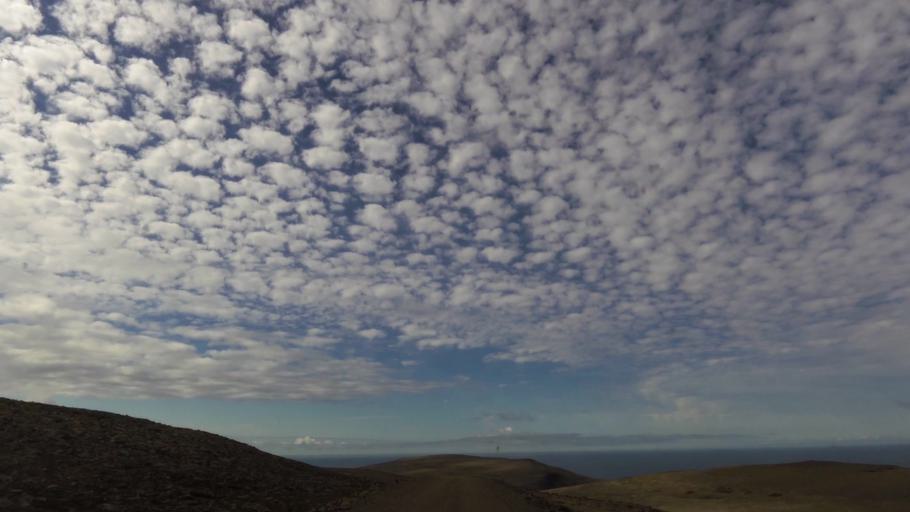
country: IS
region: West
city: Olafsvik
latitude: 65.6209
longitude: -24.2782
